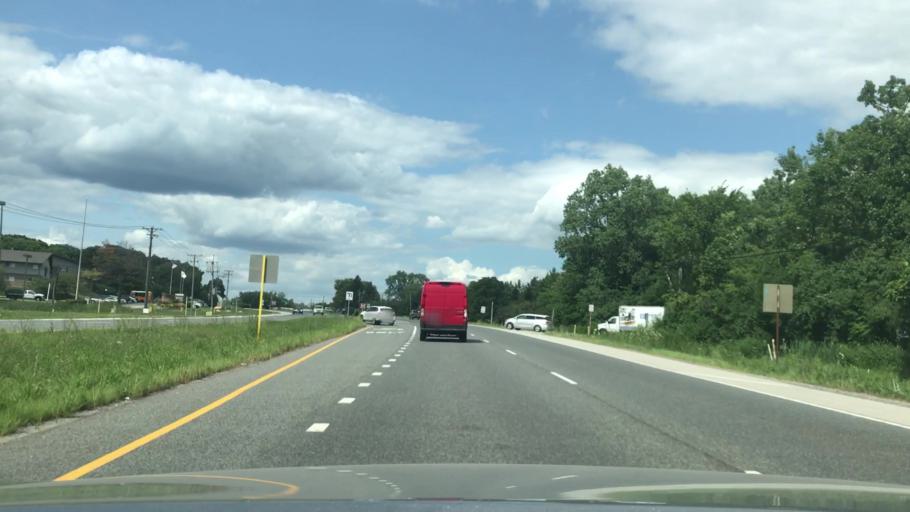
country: US
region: Illinois
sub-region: DuPage County
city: Burr Ridge
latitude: 41.7179
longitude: -87.9442
